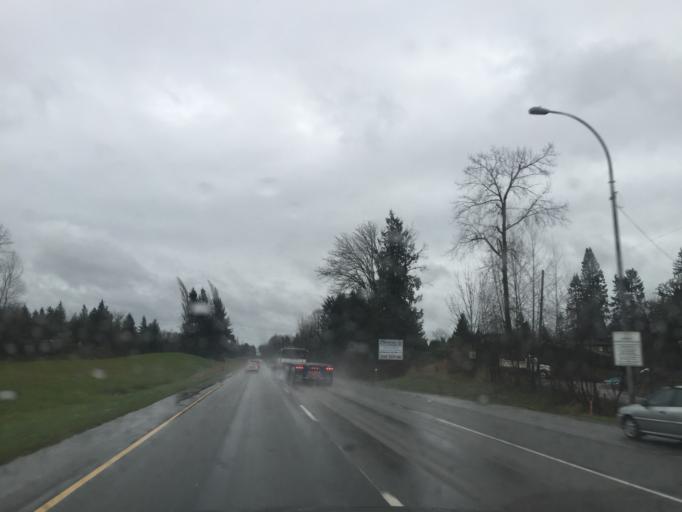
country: CA
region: British Columbia
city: Walnut Grove
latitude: 49.1470
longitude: -122.6090
